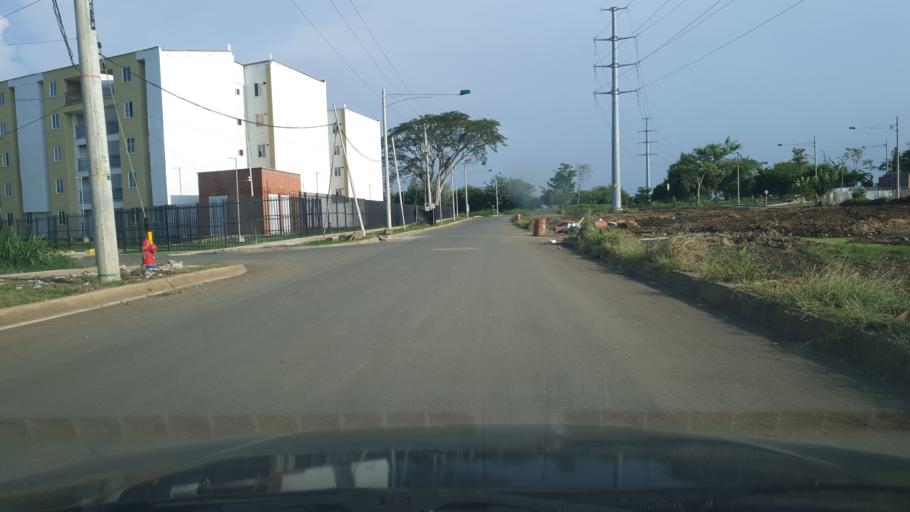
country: CO
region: Valle del Cauca
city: Jamundi
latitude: 3.3458
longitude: -76.5145
